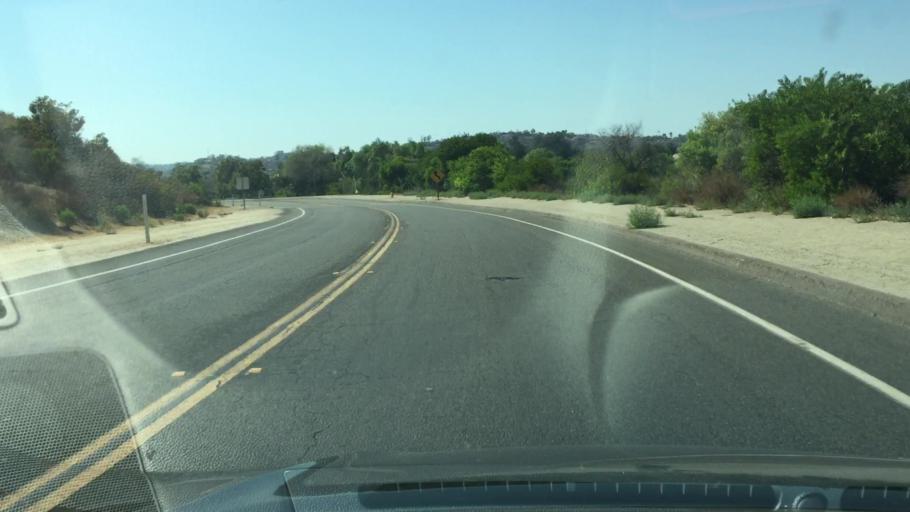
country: US
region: California
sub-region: San Diego County
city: Jamul
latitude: 32.7381
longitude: -116.8942
